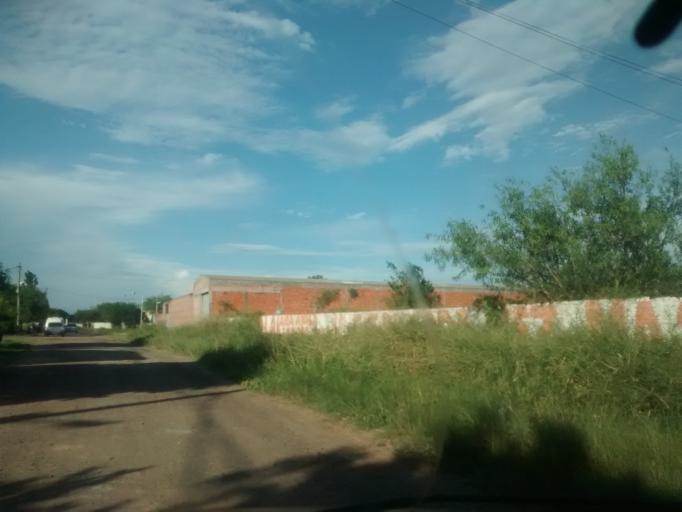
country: AR
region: Chaco
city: Fontana
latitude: -27.4543
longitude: -59.0204
